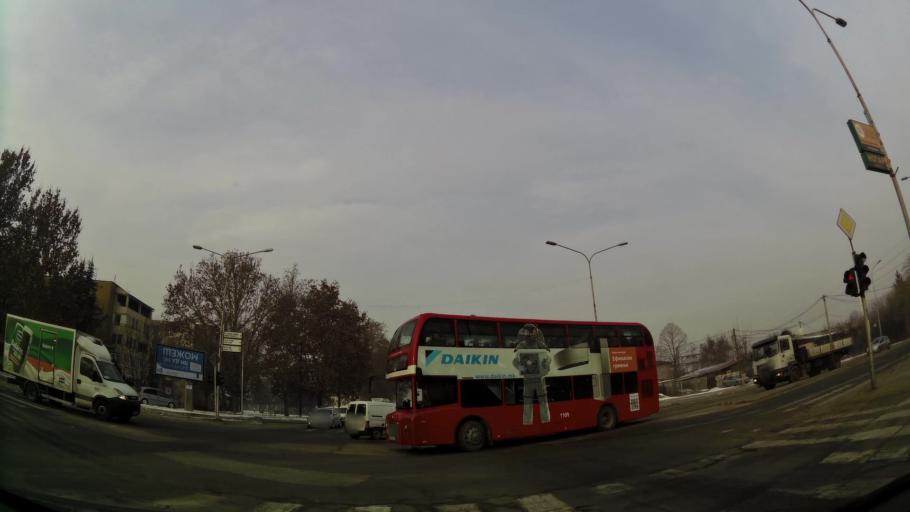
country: MK
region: Butel
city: Butel
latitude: 42.0249
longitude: 21.4448
